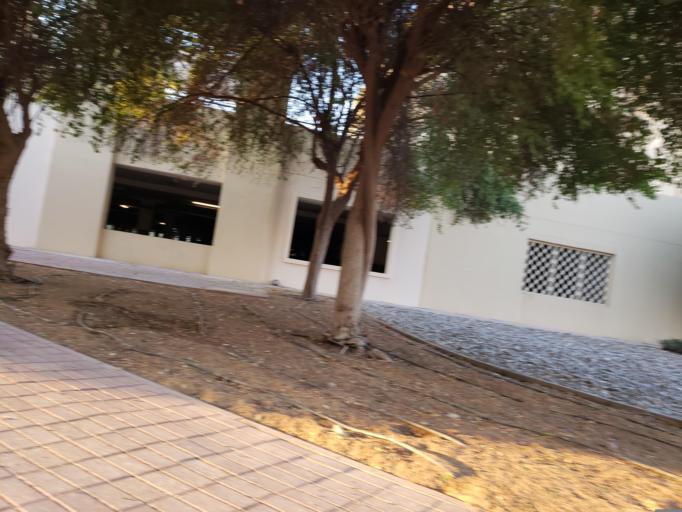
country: AE
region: Dubai
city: Dubai
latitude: 25.0032
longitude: 55.2501
